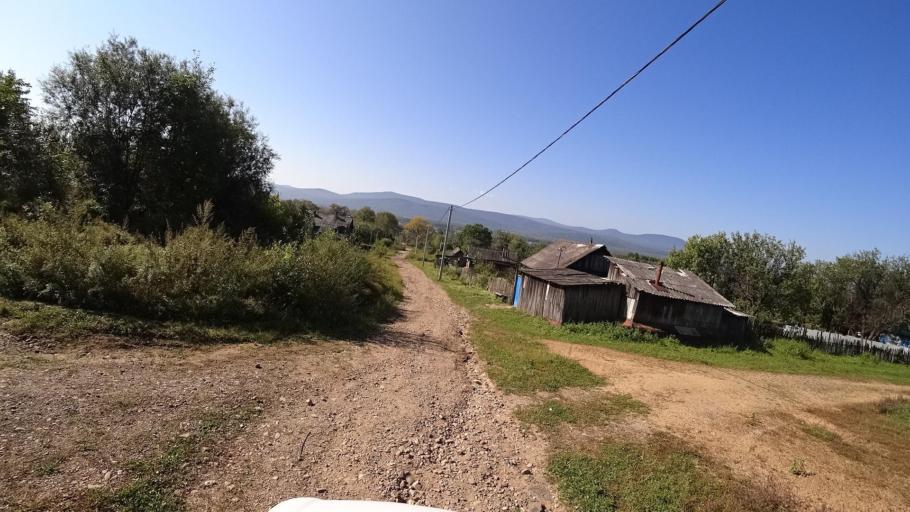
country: RU
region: Jewish Autonomous Oblast
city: Bira
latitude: 49.0069
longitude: 132.4676
